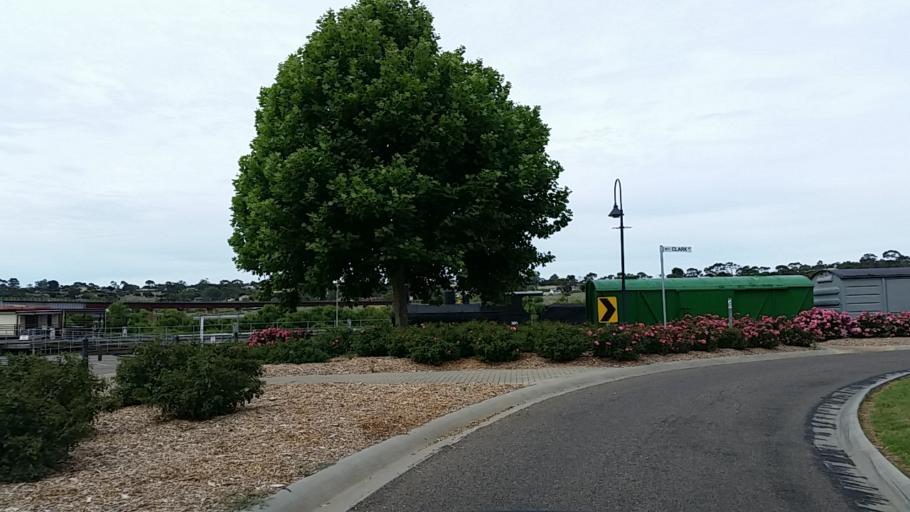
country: AU
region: South Australia
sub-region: Murray Bridge
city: Murray Bridge
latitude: -35.1182
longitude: 139.2810
